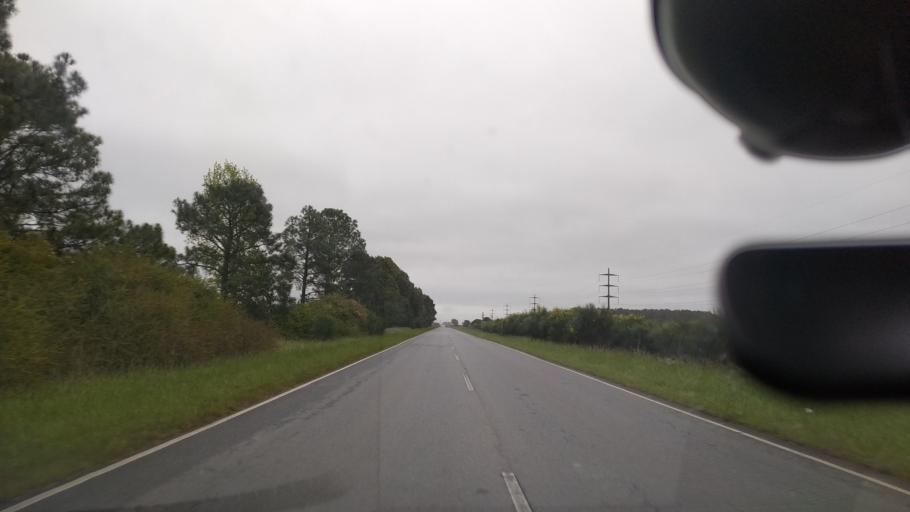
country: AR
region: Buenos Aires
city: Veronica
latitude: -35.3744
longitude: -57.3779
